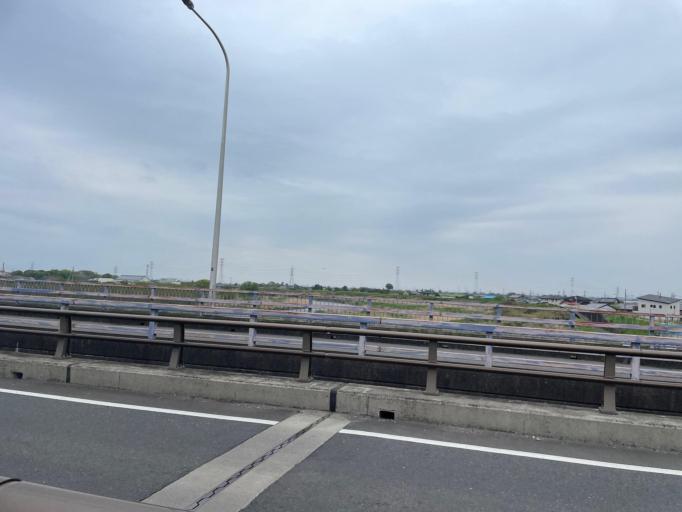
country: JP
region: Gunma
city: Sakai-nakajima
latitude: 36.2729
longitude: 139.2373
